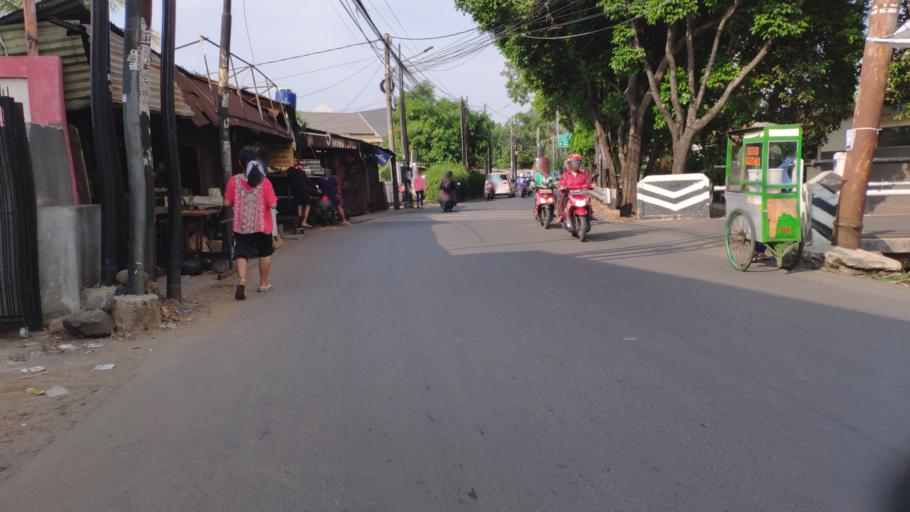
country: ID
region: West Java
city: Pamulang
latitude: -6.3138
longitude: 106.7957
